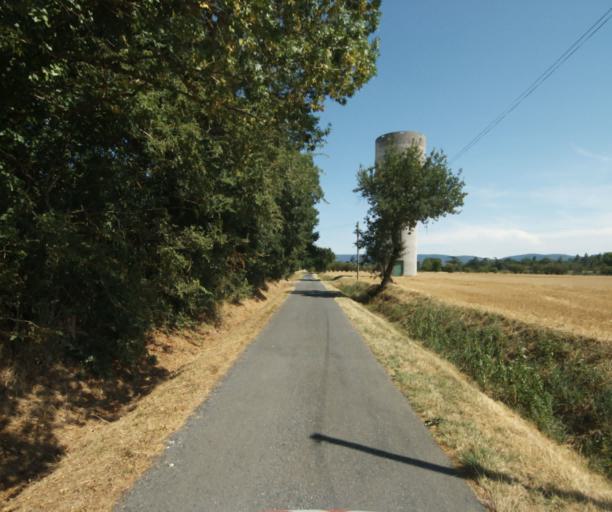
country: FR
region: Midi-Pyrenees
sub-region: Departement de la Haute-Garonne
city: Revel
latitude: 43.5001
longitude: 1.9990
